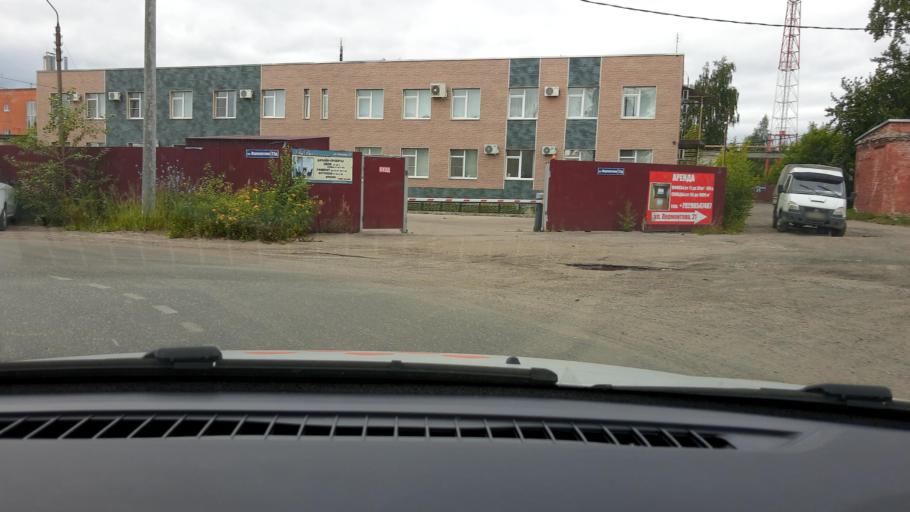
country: RU
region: Nizjnij Novgorod
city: Pyra
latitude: 56.2633
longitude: 43.3979
